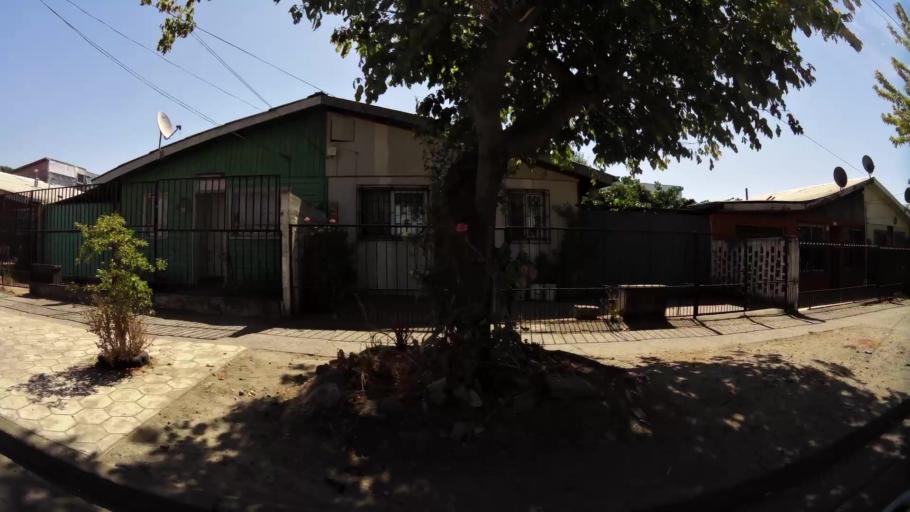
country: CL
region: Maule
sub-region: Provincia de Talca
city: Talca
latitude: -35.4439
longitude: -71.6536
